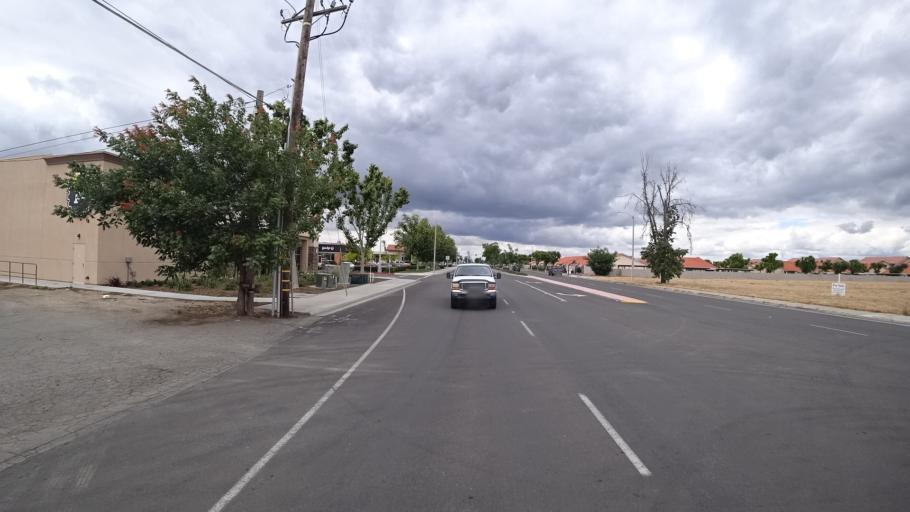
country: US
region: California
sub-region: Kings County
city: Hanford
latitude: 36.3280
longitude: -119.6767
